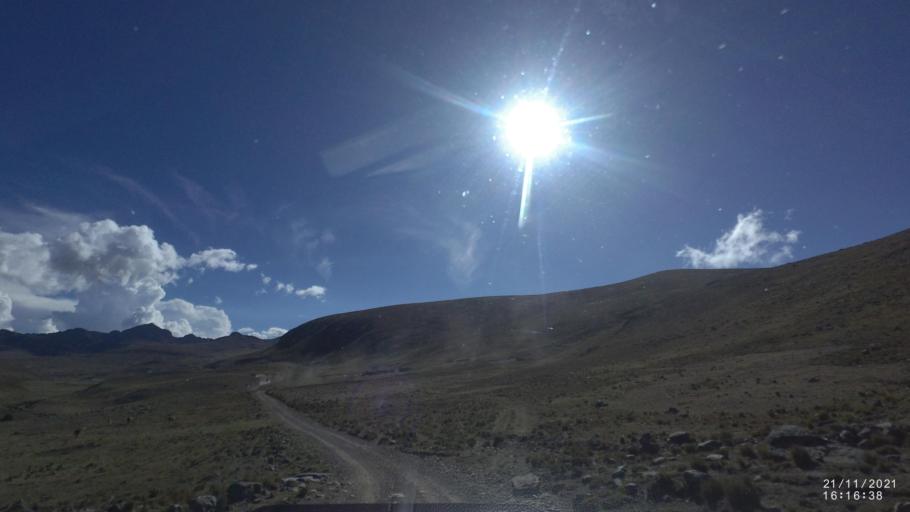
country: BO
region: Cochabamba
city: Cochabamba
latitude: -17.0003
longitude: -66.2795
